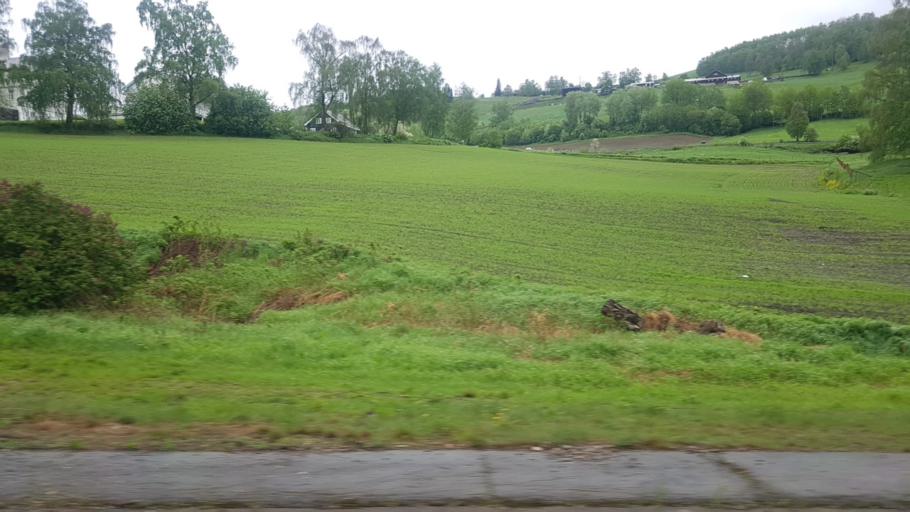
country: NO
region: Oppland
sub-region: Sor-Fron
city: Hundorp
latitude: 61.5568
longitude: 9.9419
